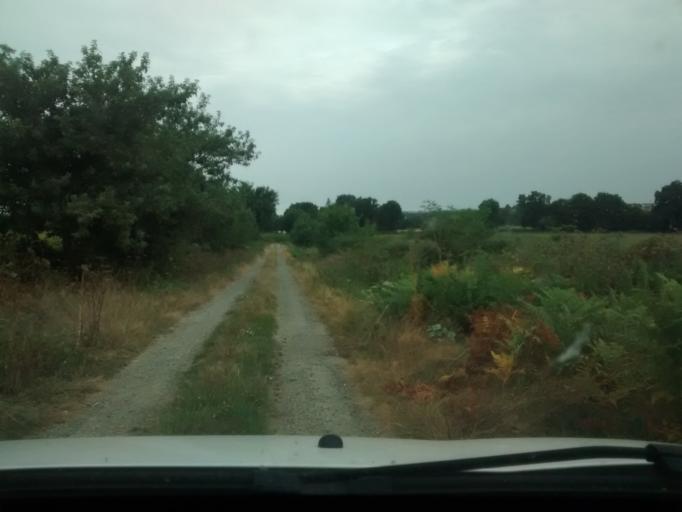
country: FR
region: Brittany
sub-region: Departement d'Ille-et-Vilaine
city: Chantepie
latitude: 48.0958
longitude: -1.5961
